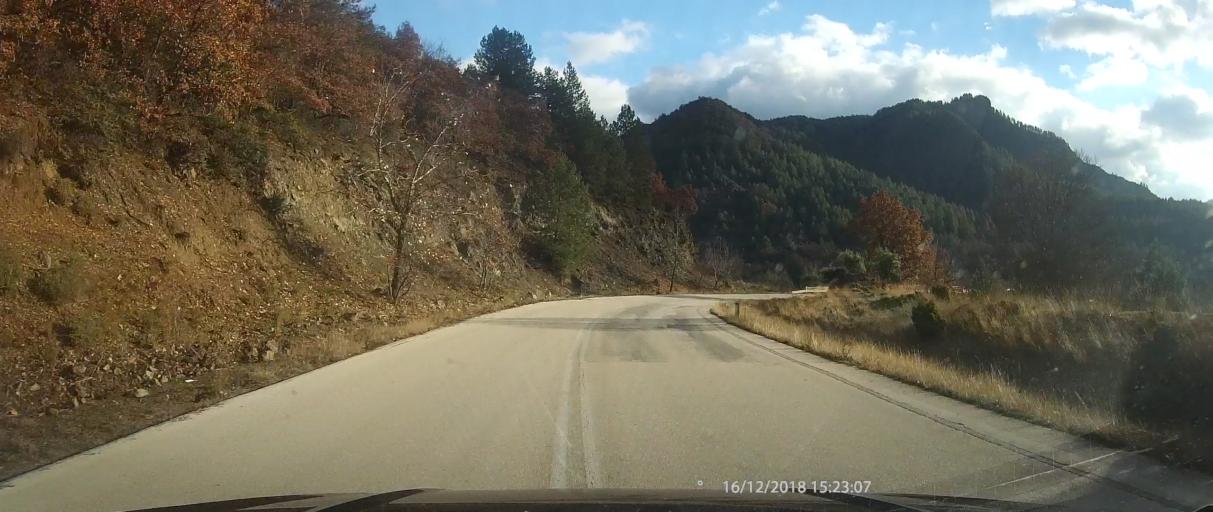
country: GR
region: Epirus
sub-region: Nomos Ioanninon
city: Konitsa
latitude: 40.1481
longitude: 20.8094
